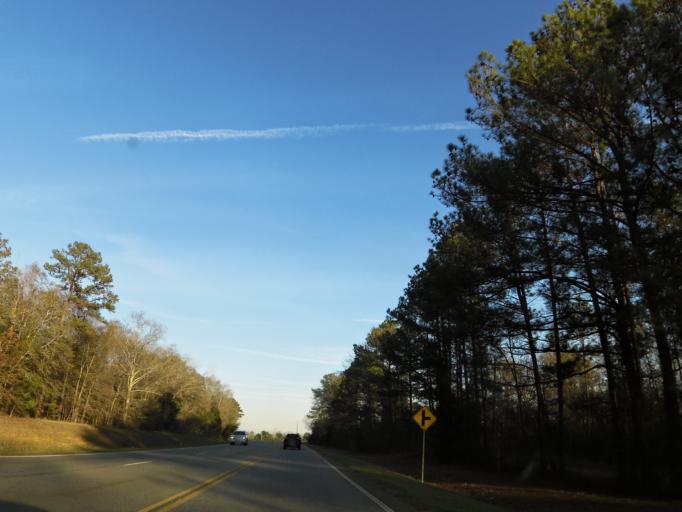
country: US
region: Georgia
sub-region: Sumter County
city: Americus
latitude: 32.0549
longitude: -84.3050
